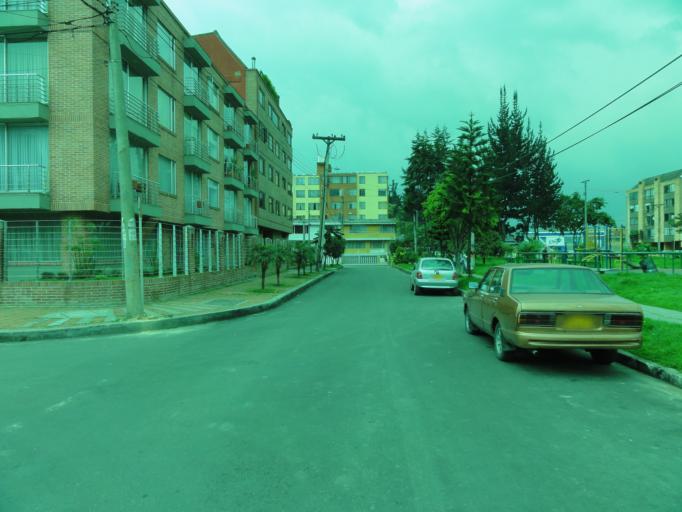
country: CO
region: Bogota D.C.
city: Bogota
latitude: 4.6513
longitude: -74.0812
